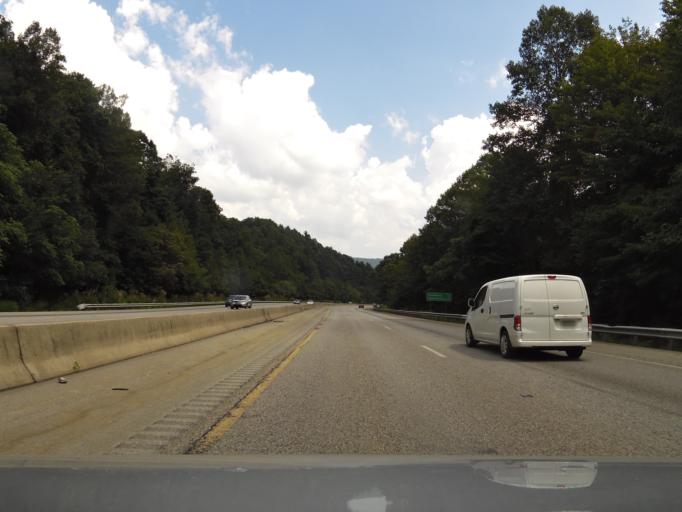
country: US
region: North Carolina
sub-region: Henderson County
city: East Flat Rock
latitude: 35.2754
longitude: -82.3836
